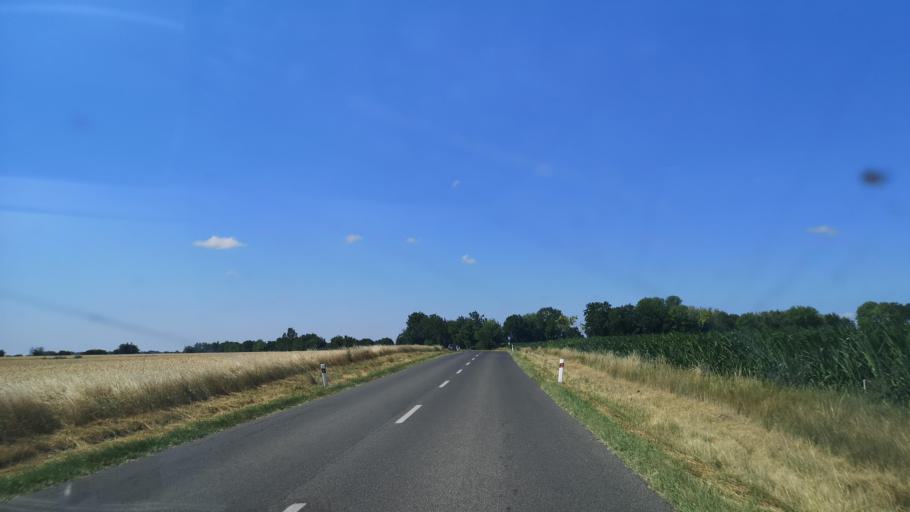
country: SK
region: Trnavsky
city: Dunajska Streda
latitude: 48.0796
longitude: 17.4924
